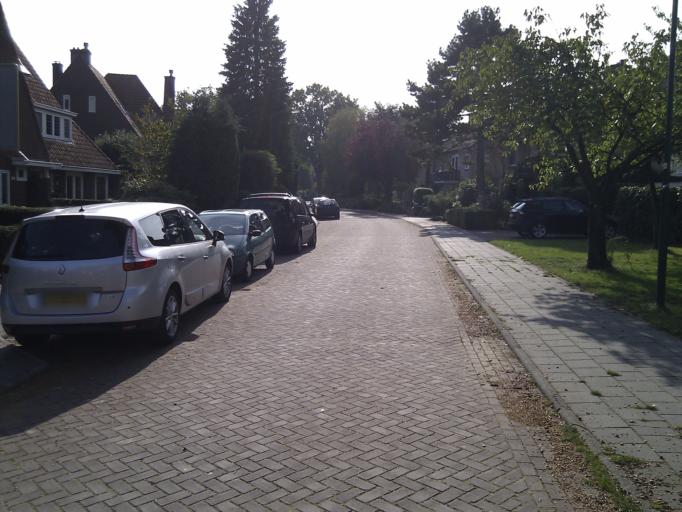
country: NL
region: Utrecht
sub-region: Gemeente De Bilt
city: De Bilt
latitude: 52.1242
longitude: 5.1992
